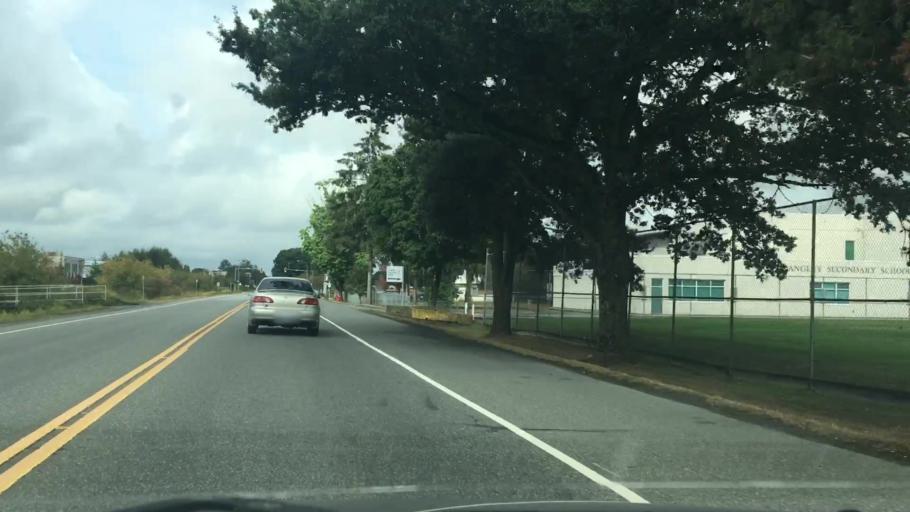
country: CA
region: British Columbia
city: Langley
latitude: 49.1045
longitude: -122.6283
